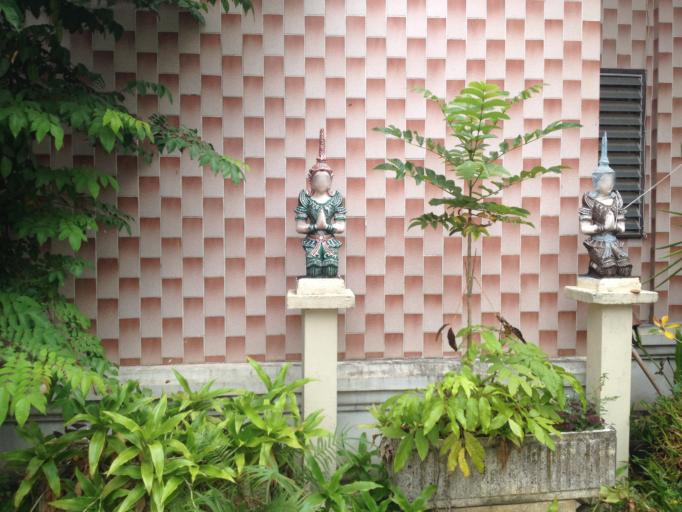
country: TH
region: Chiang Mai
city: Chiang Mai
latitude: 18.7853
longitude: 98.9814
